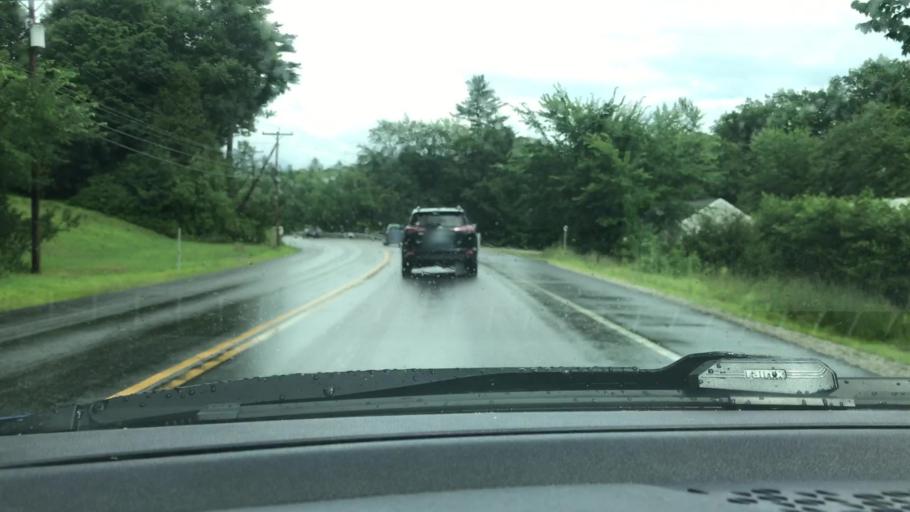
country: US
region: New Hampshire
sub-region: Merrimack County
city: Epsom
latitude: 43.2220
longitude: -71.3288
